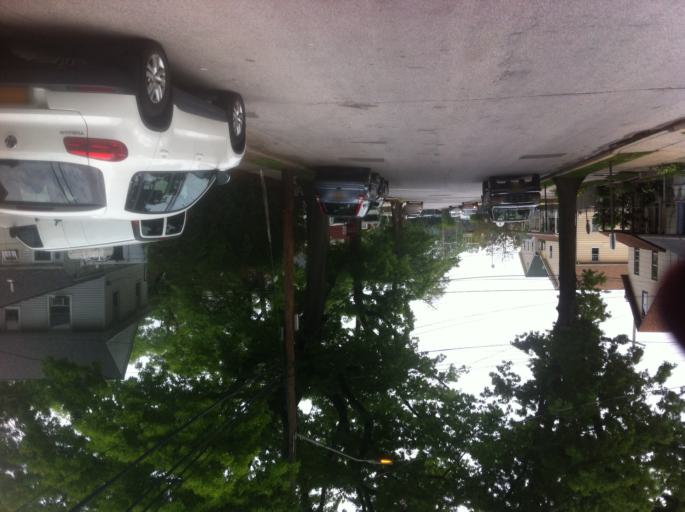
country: US
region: New York
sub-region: Nassau County
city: Oyster Bay
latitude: 40.8735
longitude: -73.5338
